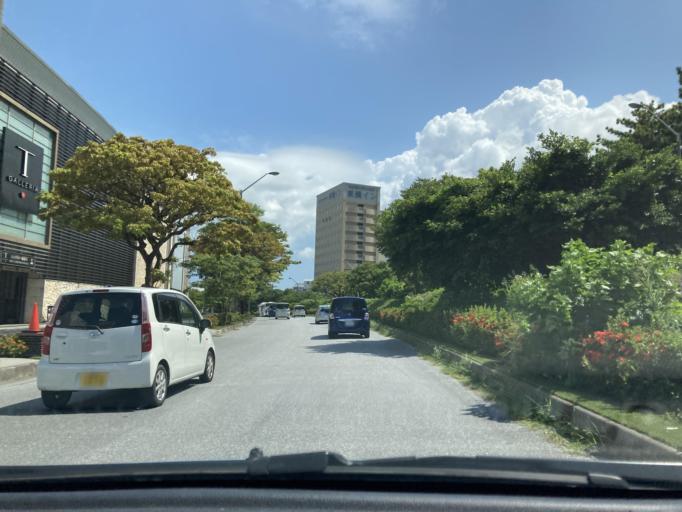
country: JP
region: Okinawa
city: Naha-shi
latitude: 26.2232
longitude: 127.6961
